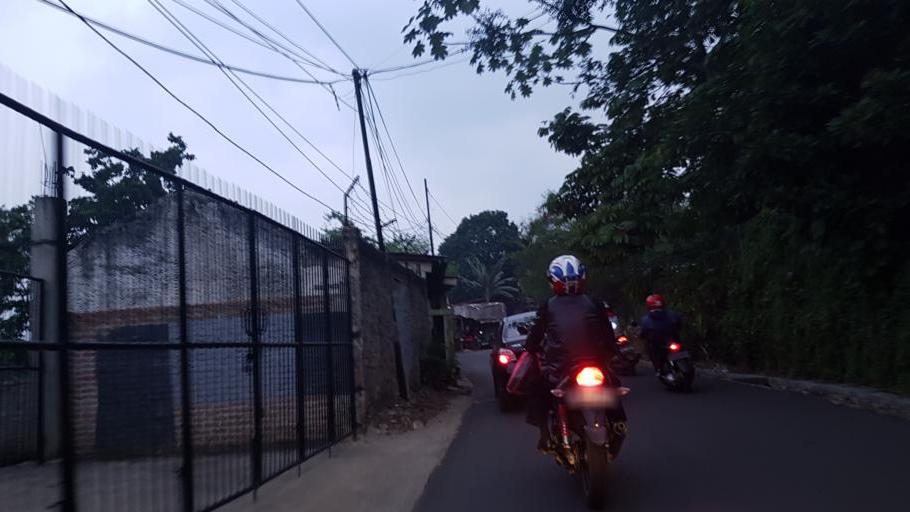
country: ID
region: West Java
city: Depok
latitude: -6.3639
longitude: 106.8000
